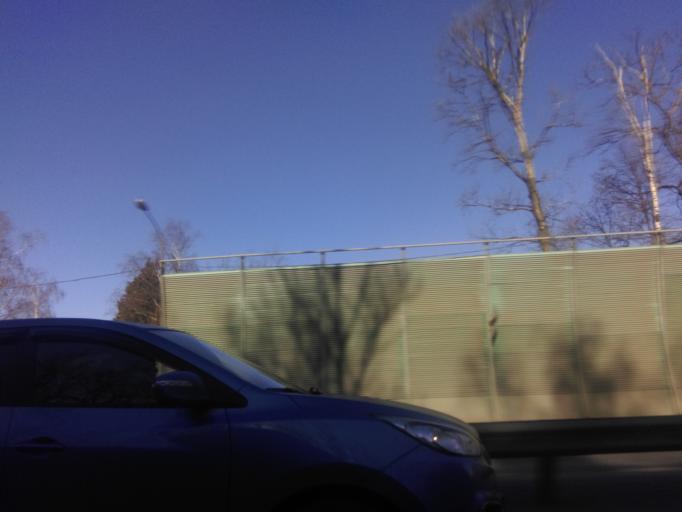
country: RU
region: Moscow
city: Novo-Peredelkino
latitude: 55.6769
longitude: 37.3192
